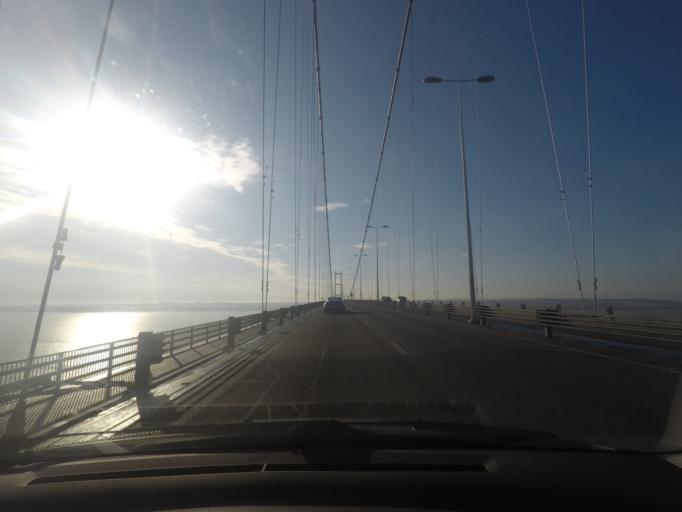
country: GB
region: England
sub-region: East Riding of Yorkshire
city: Hessle
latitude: 53.7133
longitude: -0.4499
